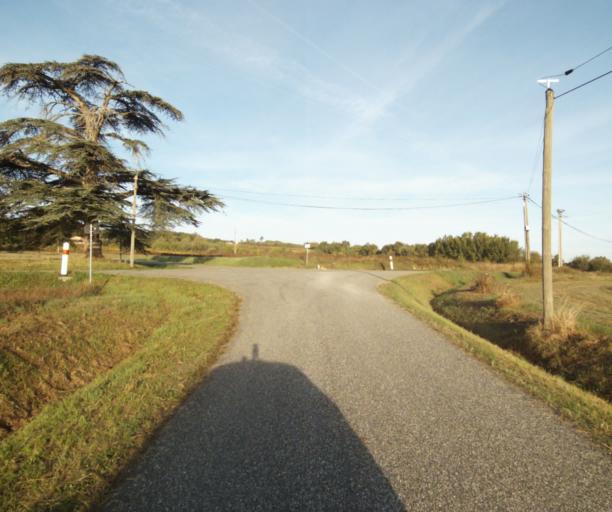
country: FR
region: Midi-Pyrenees
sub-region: Departement du Tarn-et-Garonne
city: Saint-Nauphary
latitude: 43.9467
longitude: 1.4417
